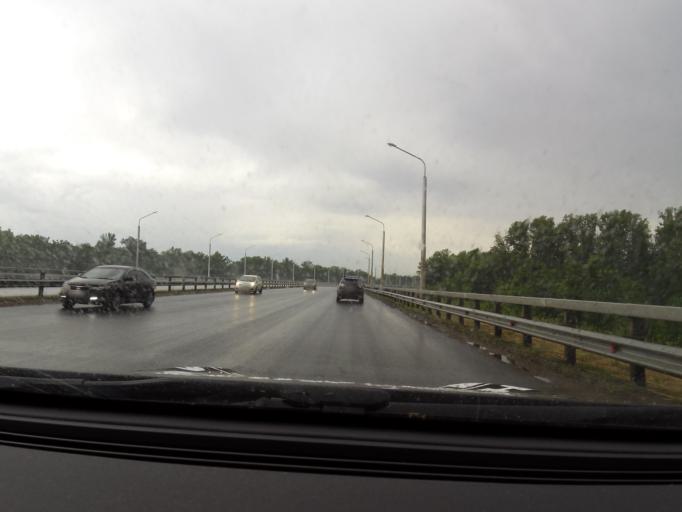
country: RU
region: Bashkortostan
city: Mikhaylovka
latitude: 54.7804
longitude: 55.9210
